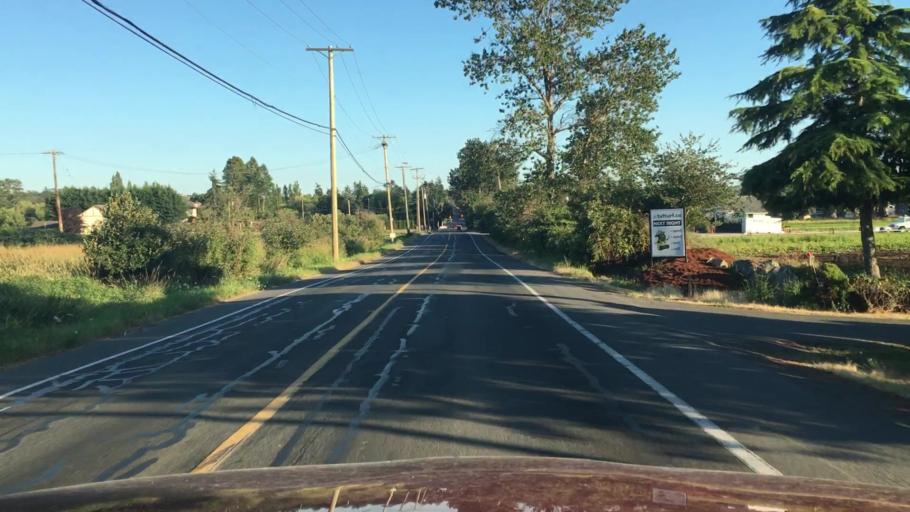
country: CA
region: British Columbia
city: Victoria
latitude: 48.4761
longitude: -123.3524
